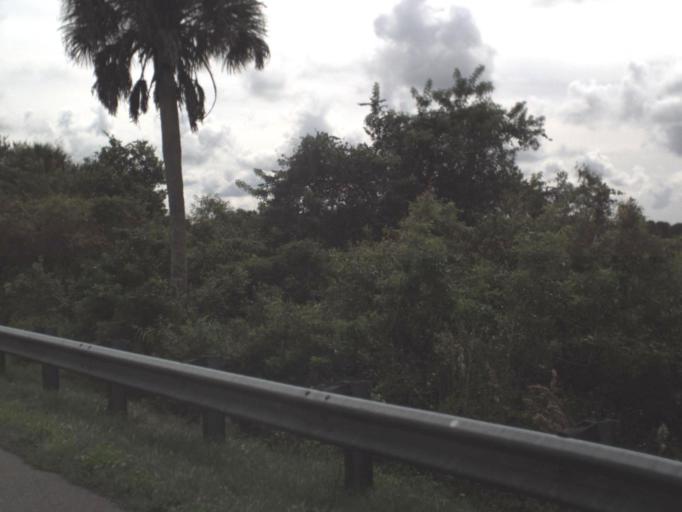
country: US
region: Florida
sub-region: Highlands County
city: Lake Placid
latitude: 27.2098
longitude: -81.1300
